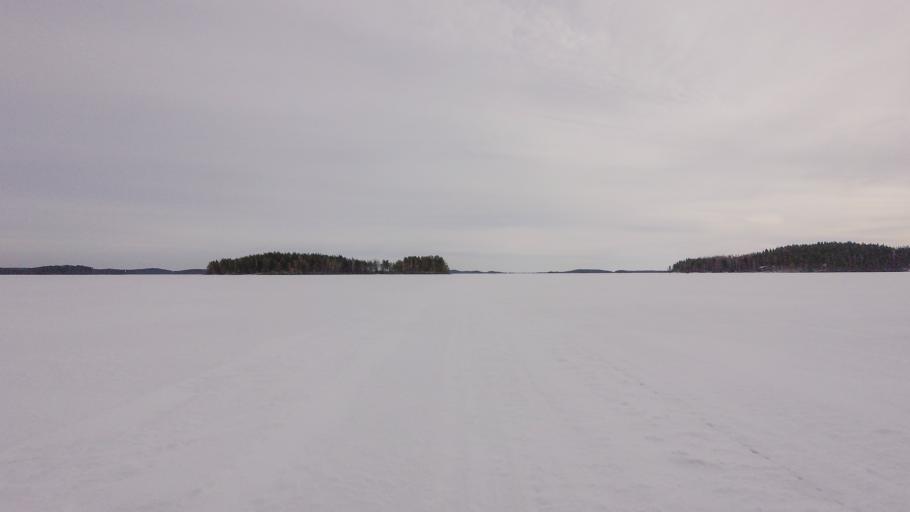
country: FI
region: Southern Savonia
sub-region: Savonlinna
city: Rantasalmi
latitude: 62.1138
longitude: 28.3682
